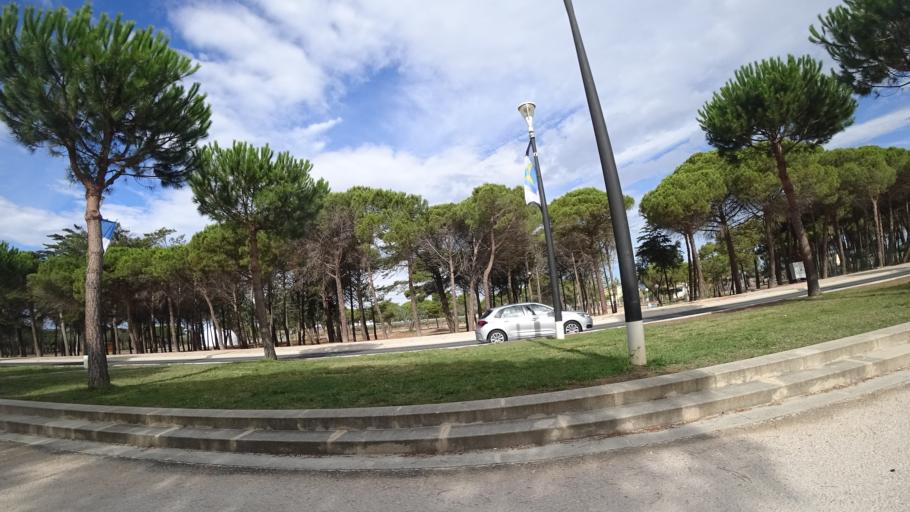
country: FR
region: Languedoc-Roussillon
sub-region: Departement des Pyrenees-Orientales
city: Le Barcares
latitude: 42.8265
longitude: 3.0356
